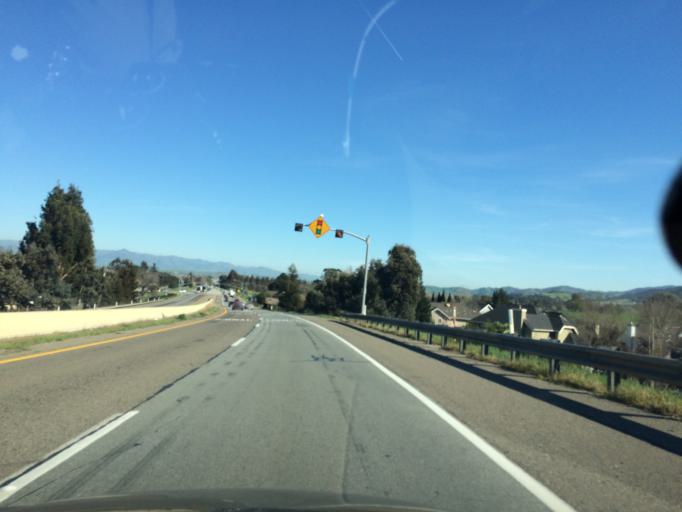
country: US
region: California
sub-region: San Benito County
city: San Juan Bautista
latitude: 36.8406
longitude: -121.5378
